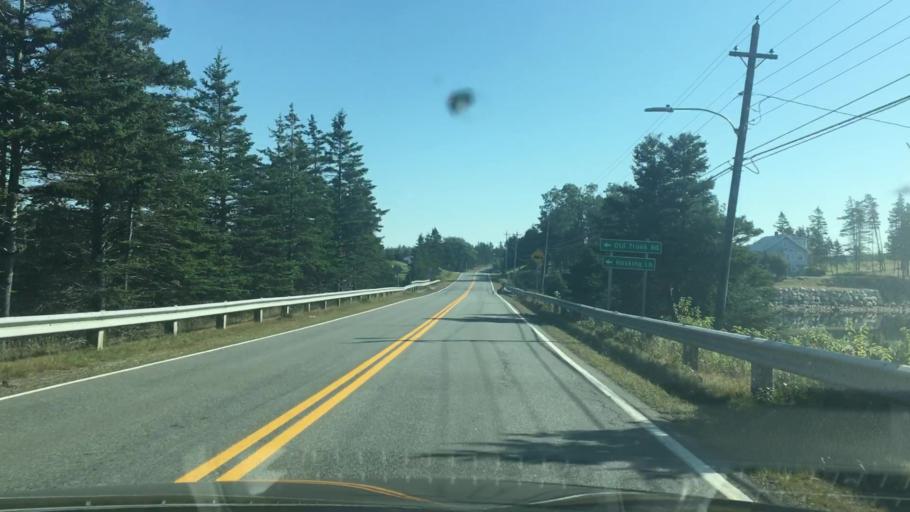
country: CA
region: Nova Scotia
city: Cole Harbour
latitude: 44.7775
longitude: -63.0136
